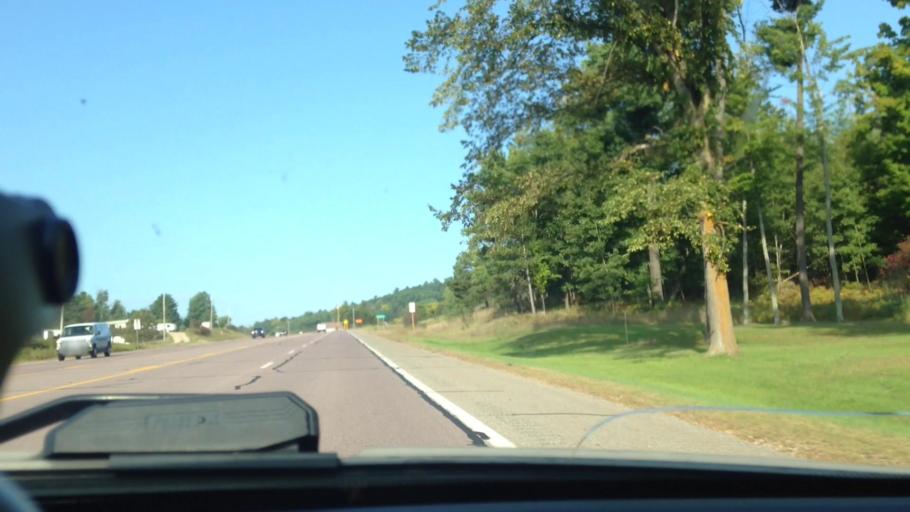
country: US
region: Michigan
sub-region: Dickinson County
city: Quinnesec
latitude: 45.8060
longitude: -87.9798
